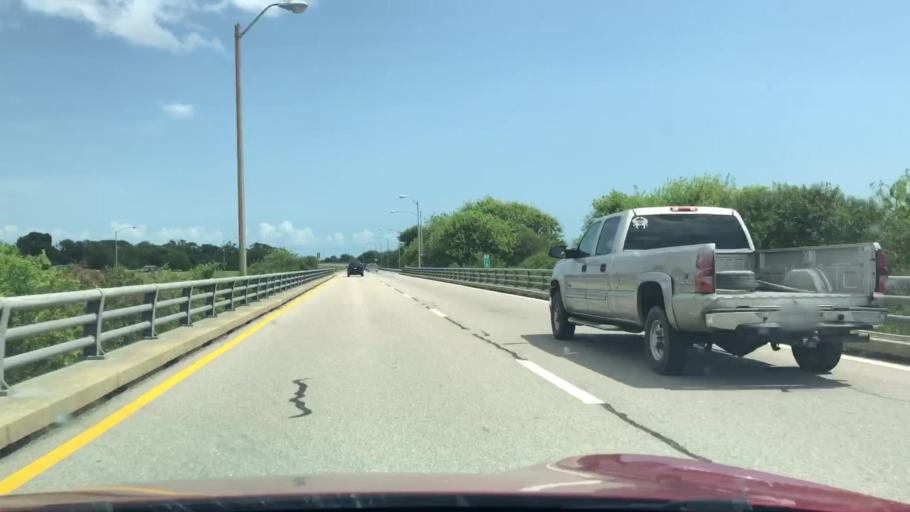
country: US
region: Virginia
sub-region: Northampton County
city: Cape Charles
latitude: 37.0916
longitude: -75.9780
